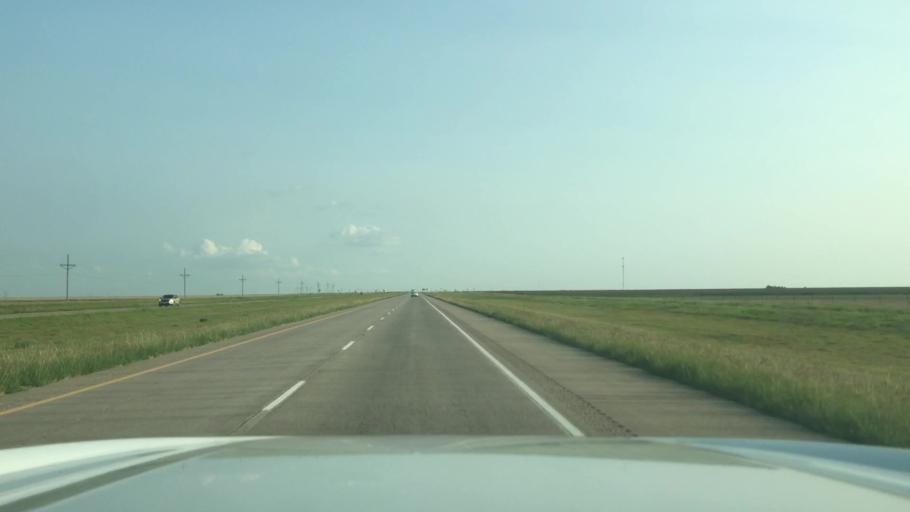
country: US
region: Texas
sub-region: Randall County
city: Canyon
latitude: 34.8634
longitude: -101.8490
